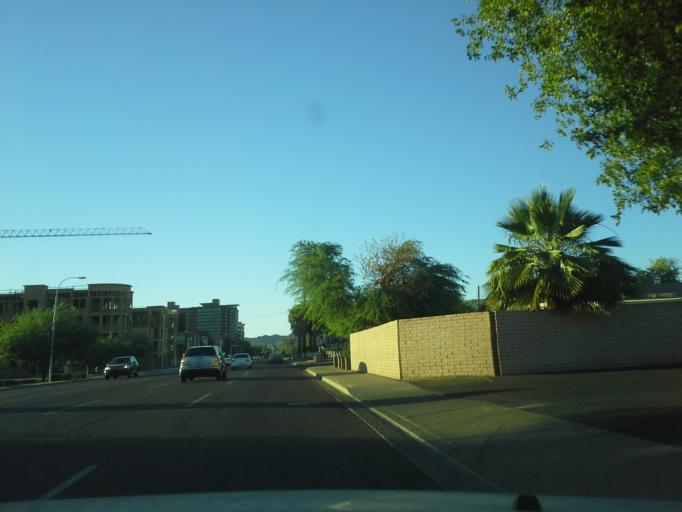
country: US
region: Arizona
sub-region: Maricopa County
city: Phoenix
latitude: 33.5029
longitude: -112.0302
